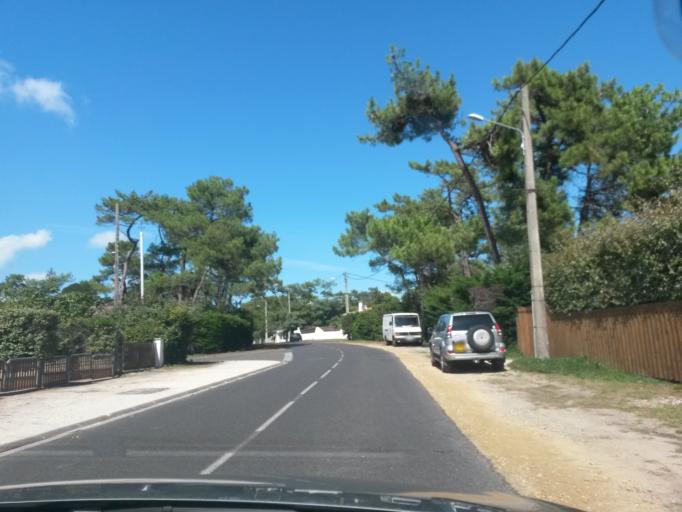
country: FR
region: Aquitaine
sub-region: Departement de la Gironde
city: Arcachon
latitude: 44.6525
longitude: -1.2491
